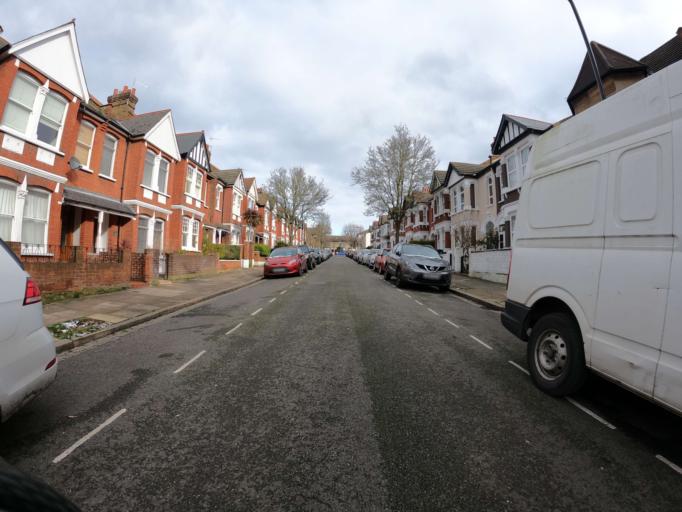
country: GB
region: England
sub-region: Greater London
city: Greenford
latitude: 51.5094
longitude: -0.3407
